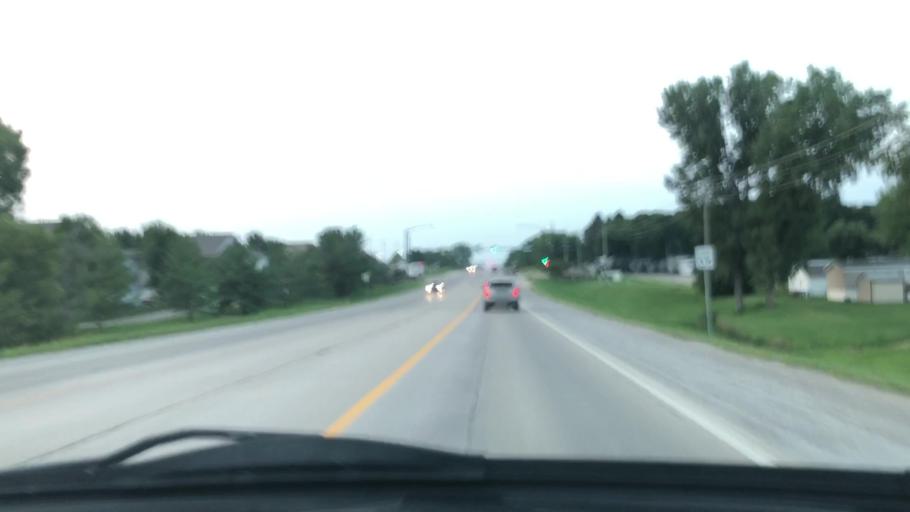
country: US
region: Iowa
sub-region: Johnson County
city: North Liberty
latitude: 41.7360
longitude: -91.6076
